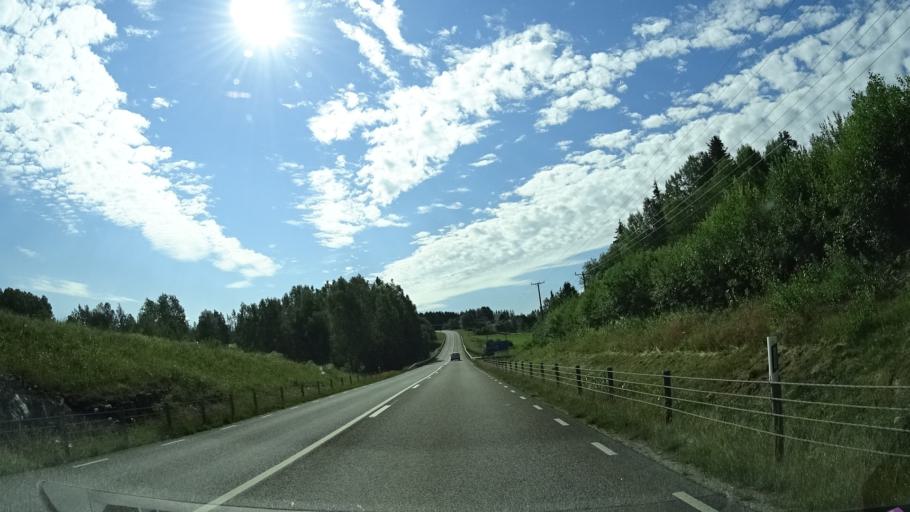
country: SE
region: Vaermland
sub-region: Arjangs Kommun
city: Arjaeng
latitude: 59.4671
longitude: 12.0036
